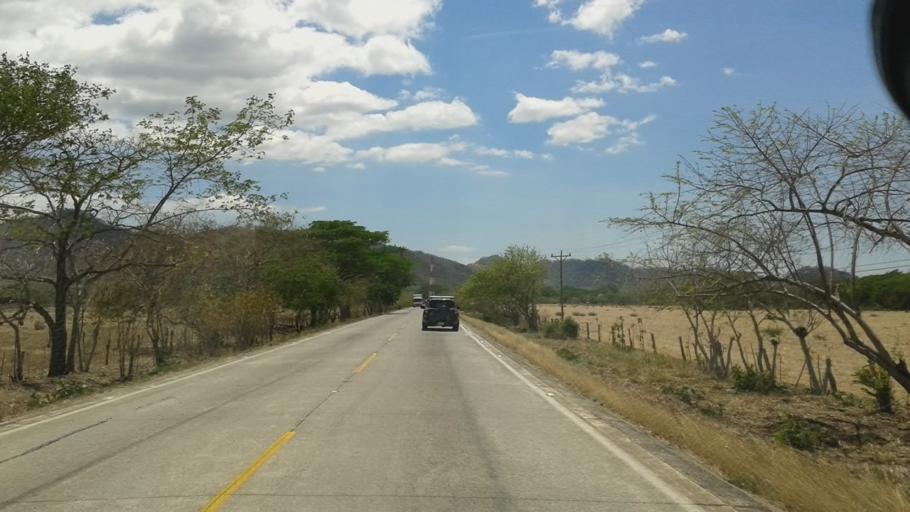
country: CR
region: Guanacaste
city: Juntas
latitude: 10.2341
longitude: -85.0849
